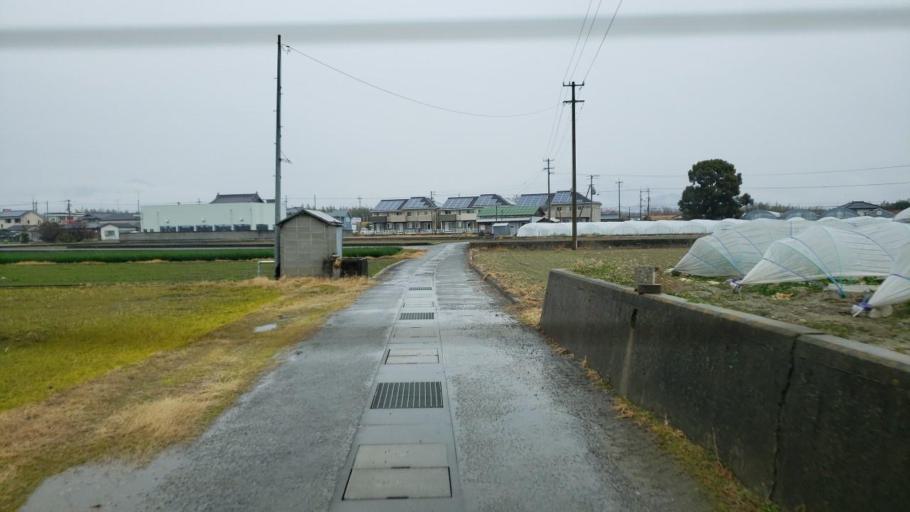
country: JP
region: Tokushima
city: Kamojimacho-jogejima
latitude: 34.0608
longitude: 134.2840
